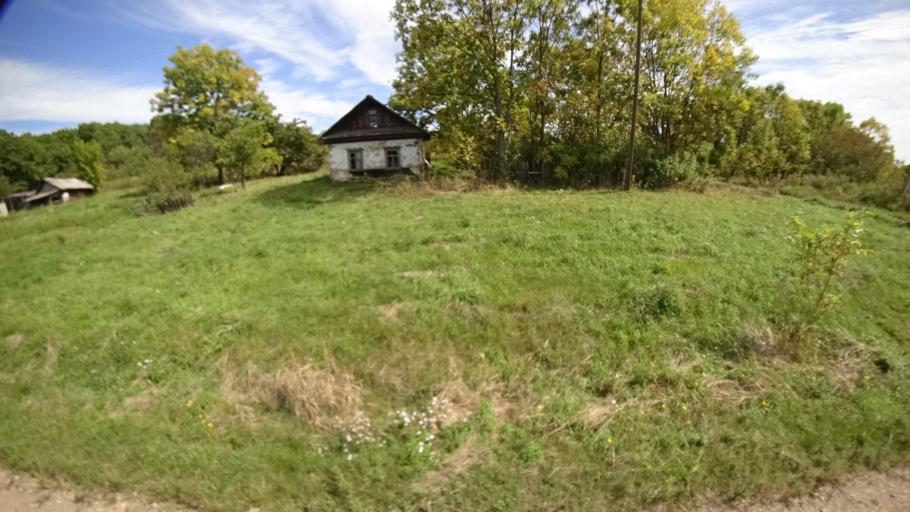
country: RU
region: Primorskiy
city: Yakovlevka
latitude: 44.6482
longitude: 133.5879
